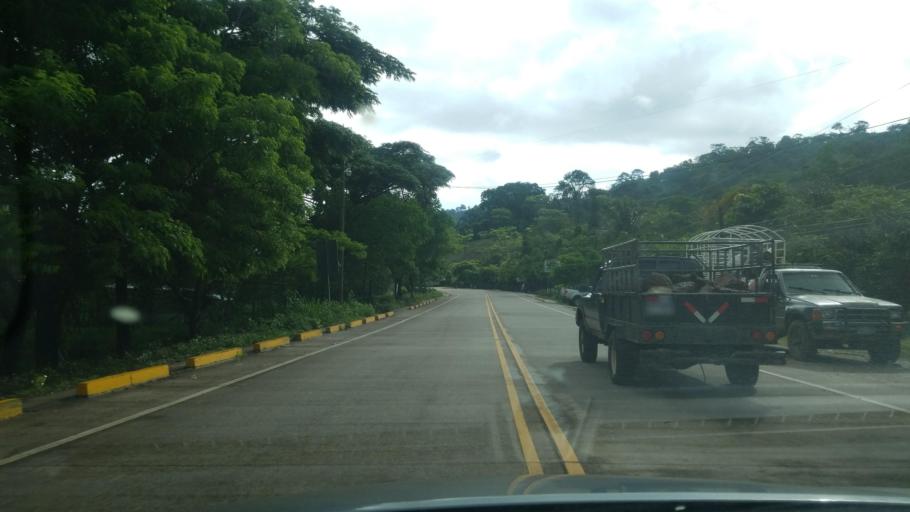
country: HN
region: Copan
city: Copan
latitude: 14.8425
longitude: -89.1710
